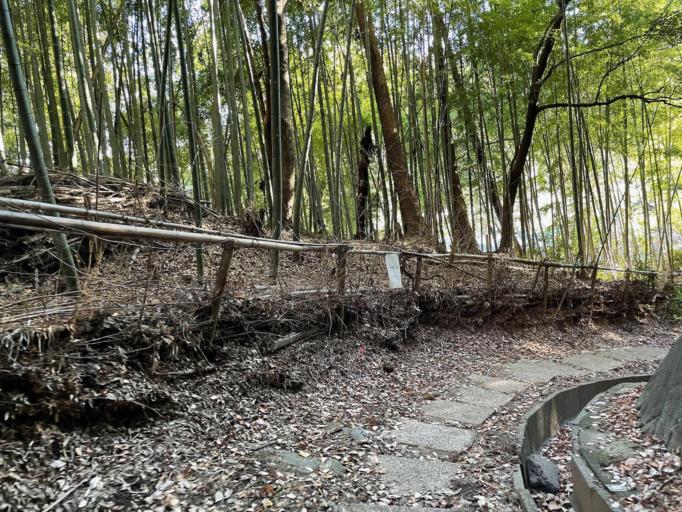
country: JP
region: Tokyo
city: Chofugaoka
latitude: 35.6301
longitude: 139.5214
